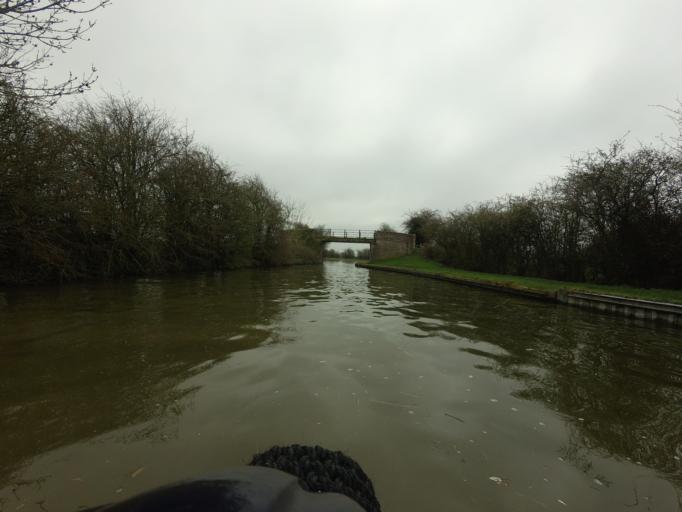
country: GB
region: England
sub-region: Buckinghamshire
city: Cheddington
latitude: 51.8797
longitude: -0.6588
